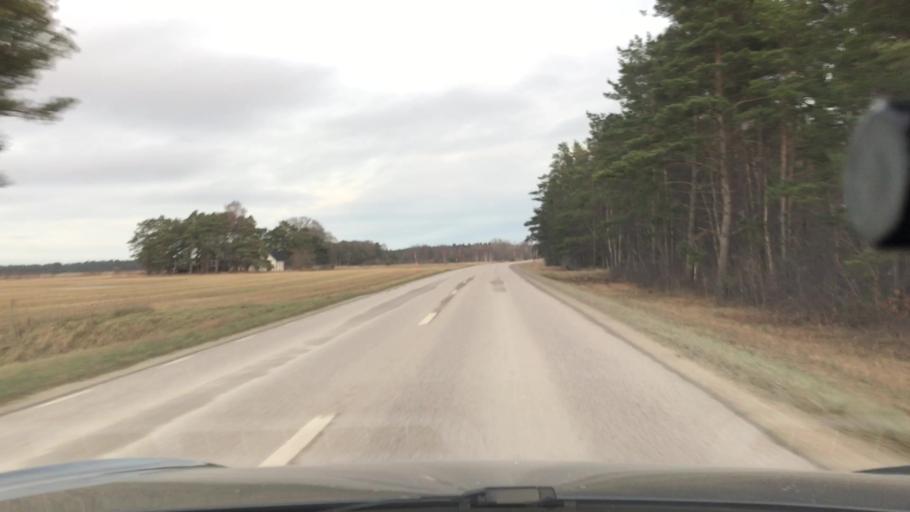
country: SE
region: Gotland
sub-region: Gotland
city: Slite
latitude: 57.7168
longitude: 18.5524
